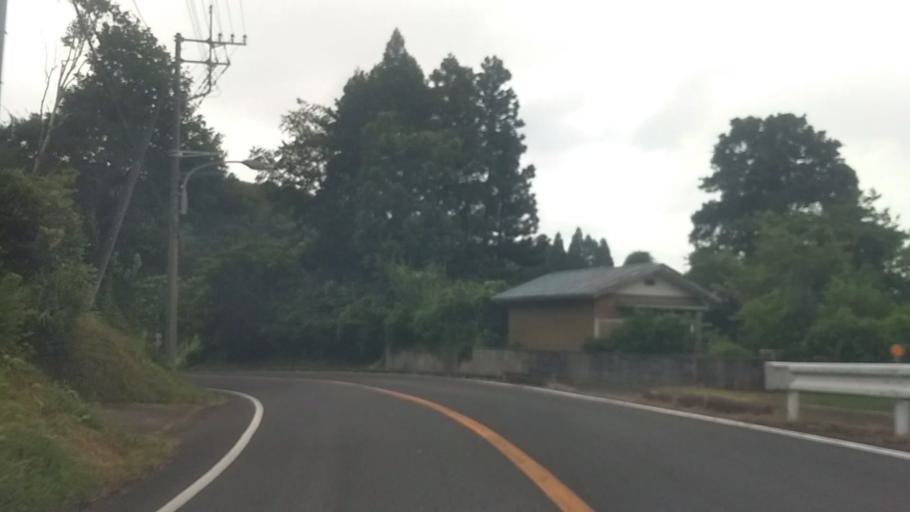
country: JP
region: Chiba
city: Katsuura
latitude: 35.2462
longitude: 140.1939
